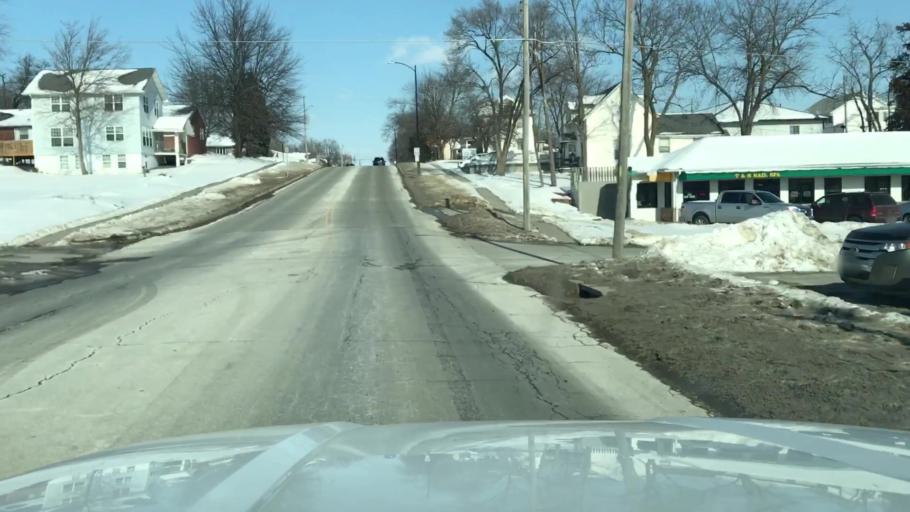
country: US
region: Missouri
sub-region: Nodaway County
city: Maryville
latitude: 40.3411
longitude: -94.8730
